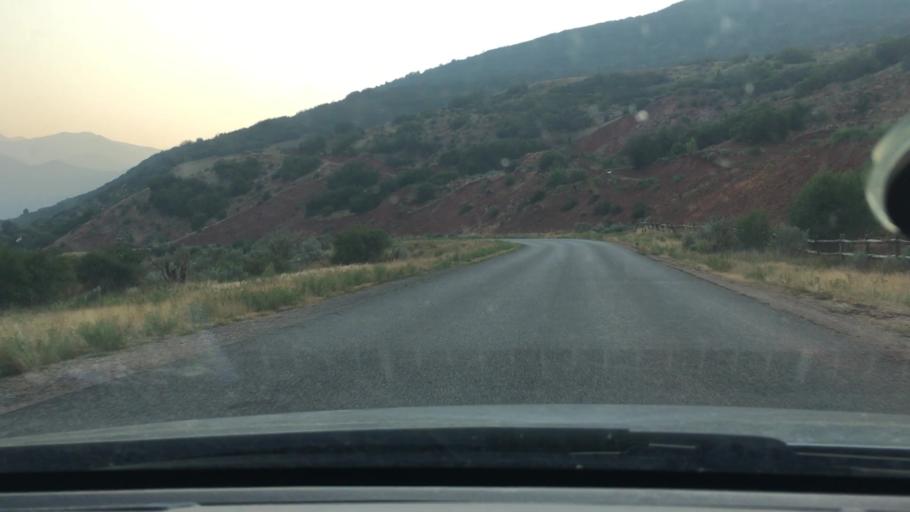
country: US
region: Utah
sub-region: Utah County
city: Mapleton
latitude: 40.0405
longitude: -111.4863
